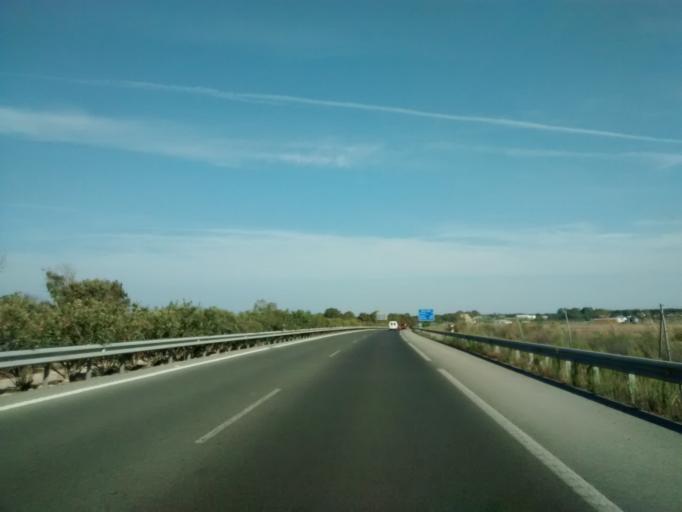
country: ES
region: Andalusia
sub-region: Provincia de Cadiz
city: Chiclana de la Frontera
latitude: 36.3635
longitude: -6.1109
